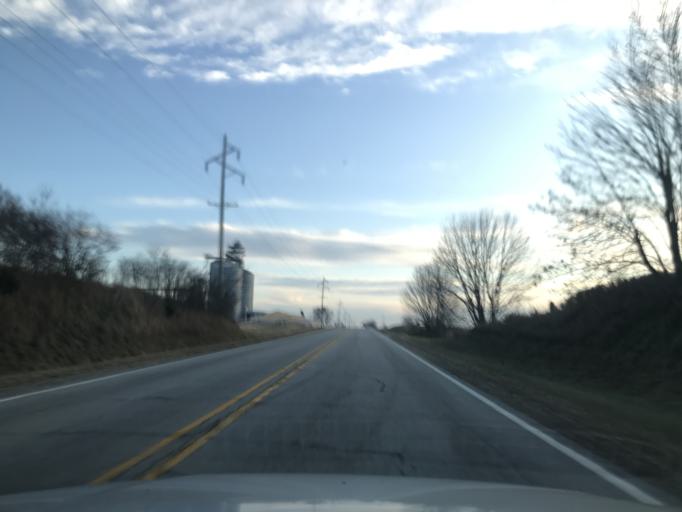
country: US
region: Illinois
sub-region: Warren County
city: Monmouth
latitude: 41.0368
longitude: -90.7460
